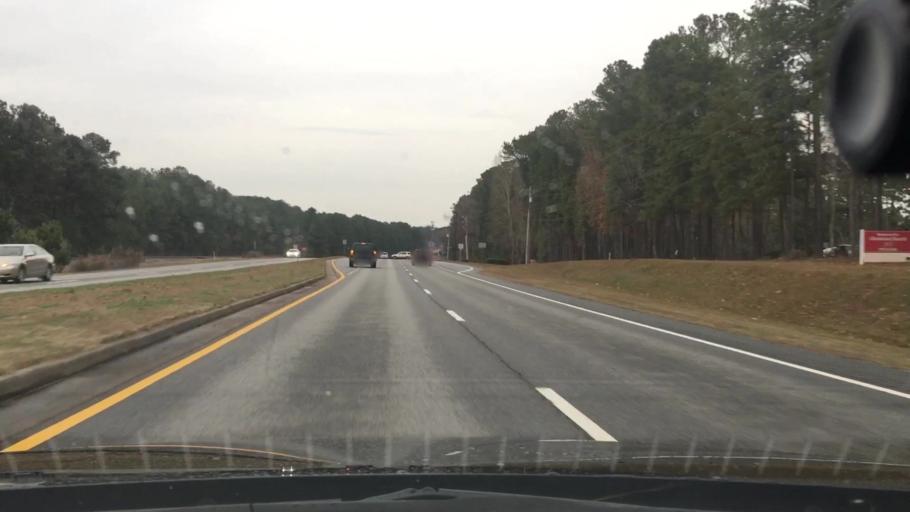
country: US
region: Georgia
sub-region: Fayette County
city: Peachtree City
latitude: 33.4186
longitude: -84.6033
